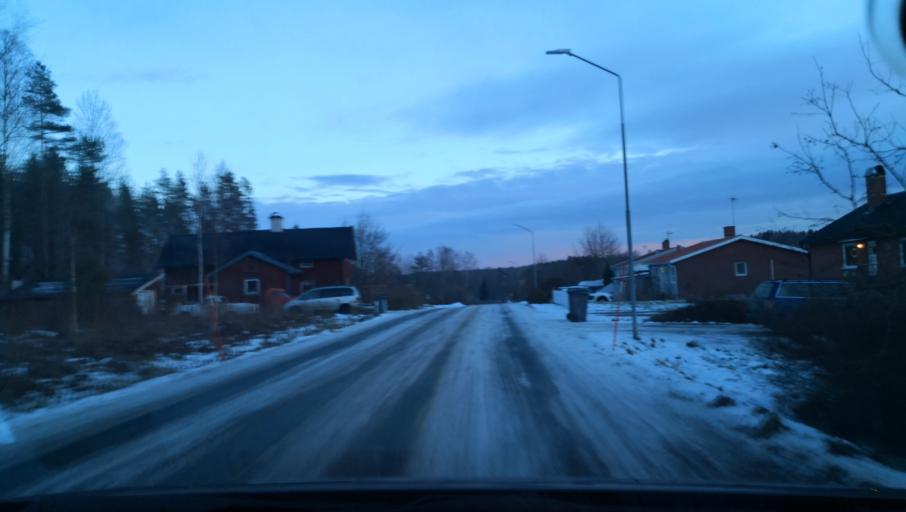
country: SE
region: Soedermanland
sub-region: Katrineholms Kommun
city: Katrineholm
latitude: 59.0918
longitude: 16.2017
